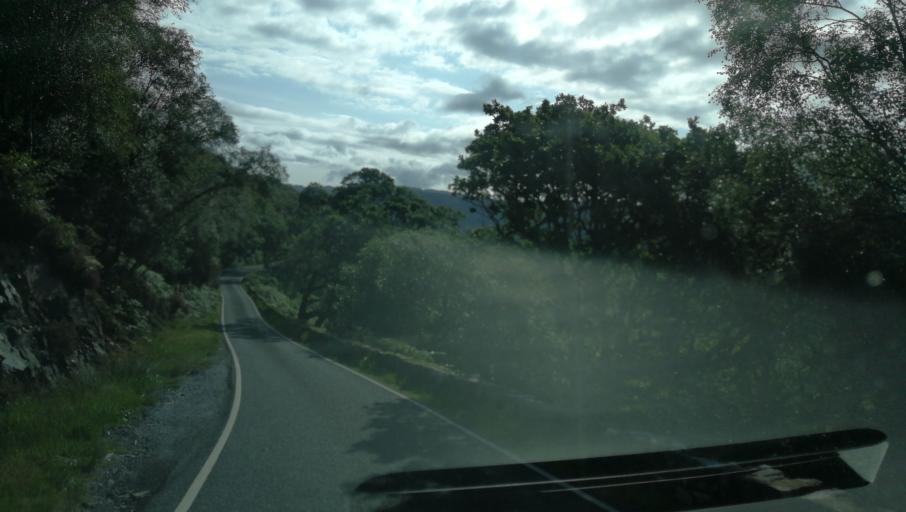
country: GB
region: Scotland
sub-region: Argyll and Bute
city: Isle Of Mull
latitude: 56.6785
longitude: -5.8453
